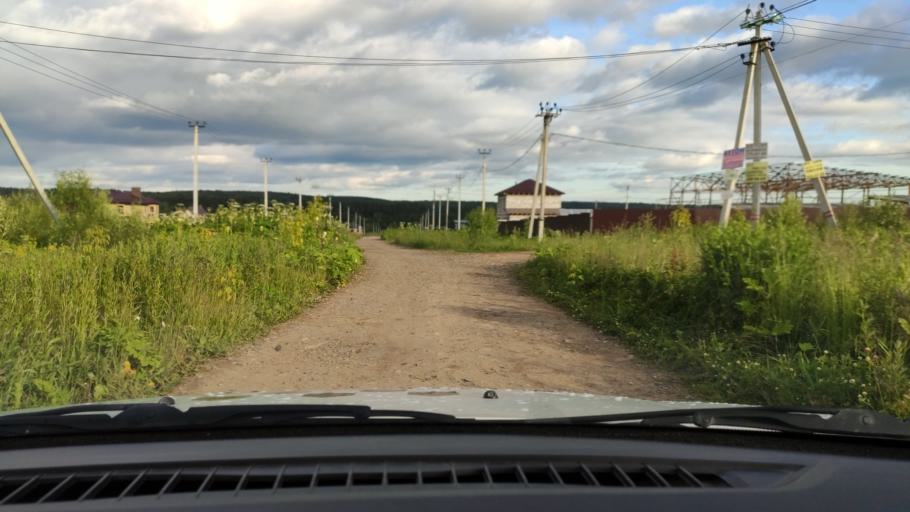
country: RU
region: Perm
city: Perm
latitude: 58.0354
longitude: 56.3796
